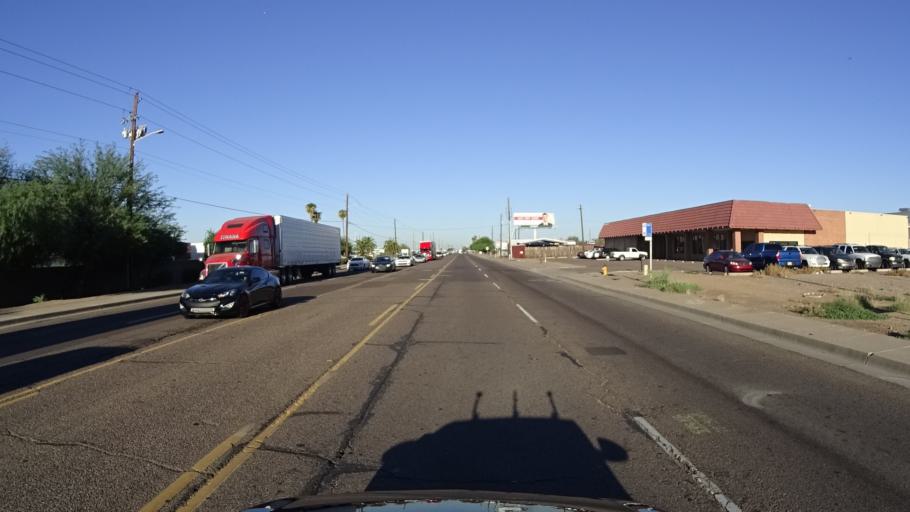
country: US
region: Arizona
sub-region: Maricopa County
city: Laveen
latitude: 33.4370
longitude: -112.1809
